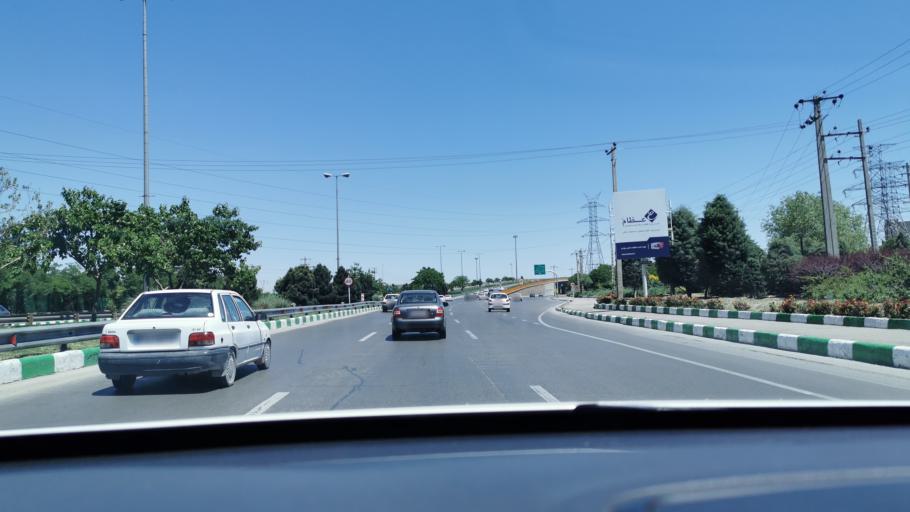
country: IR
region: Razavi Khorasan
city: Mashhad
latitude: 36.2569
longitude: 59.5934
